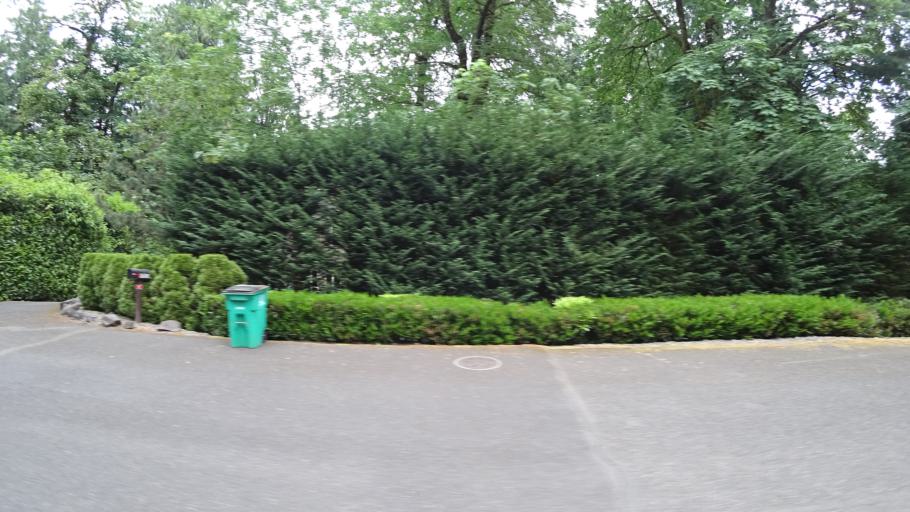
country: US
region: Oregon
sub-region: Clackamas County
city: Lake Oswego
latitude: 45.4491
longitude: -122.6905
